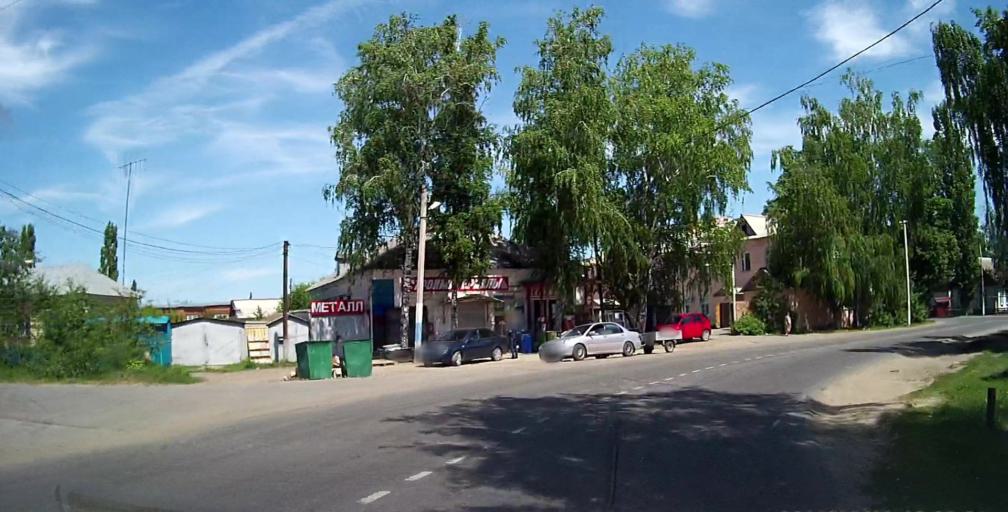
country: RU
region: Lipetsk
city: Chaplygin
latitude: 53.2457
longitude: 39.9712
